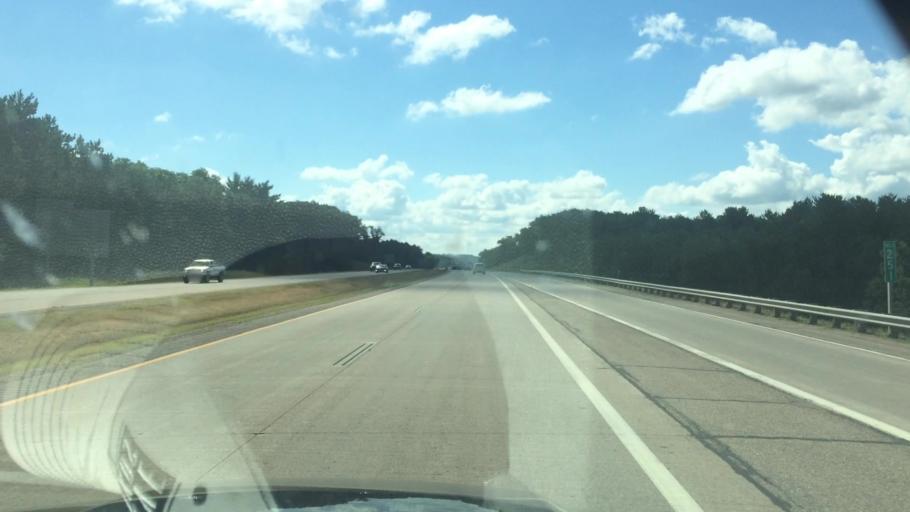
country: US
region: Wisconsin
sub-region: Waupaca County
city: Waupaca
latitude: 44.3537
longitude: -89.1124
